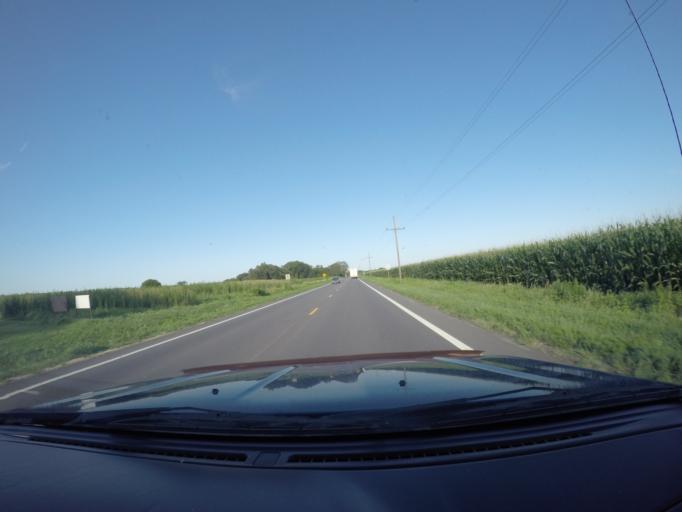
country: US
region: Kansas
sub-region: Douglas County
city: Lawrence
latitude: 39.0006
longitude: -95.2043
